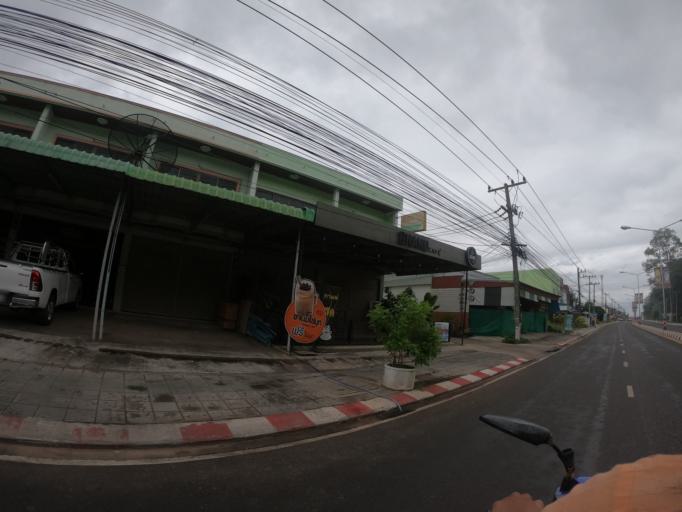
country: TH
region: Roi Et
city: Chiang Khwan
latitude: 16.1467
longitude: 103.8688
